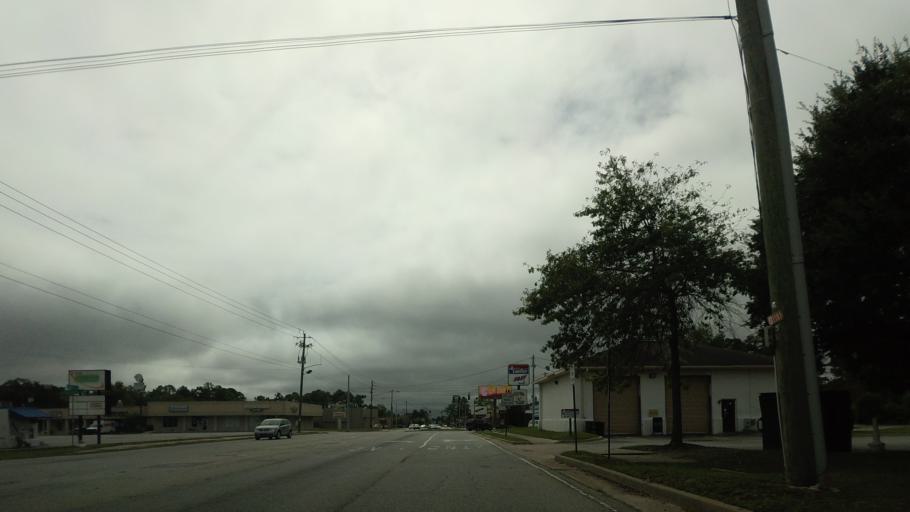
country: US
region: Georgia
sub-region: Lowndes County
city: Valdosta
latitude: 30.8585
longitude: -83.2809
